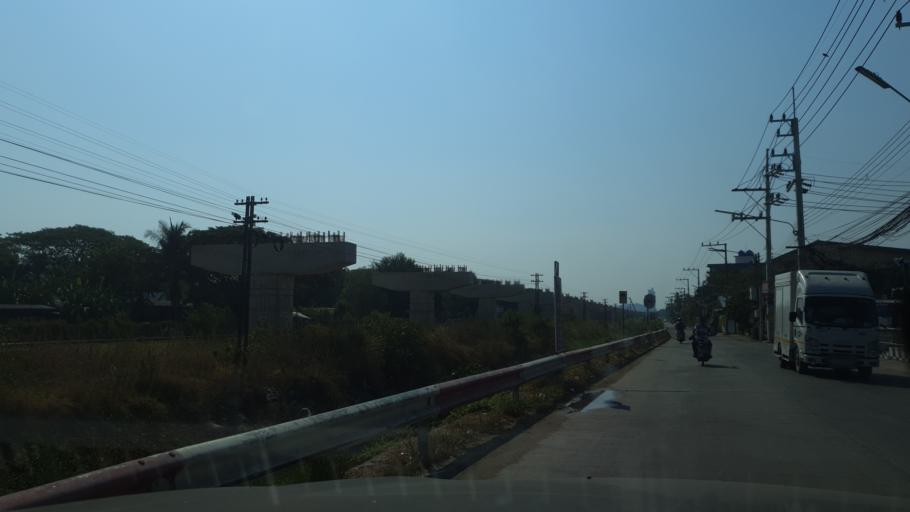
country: TH
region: Prachuap Khiri Khan
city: Hua Hin
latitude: 12.5603
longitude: 99.9561
